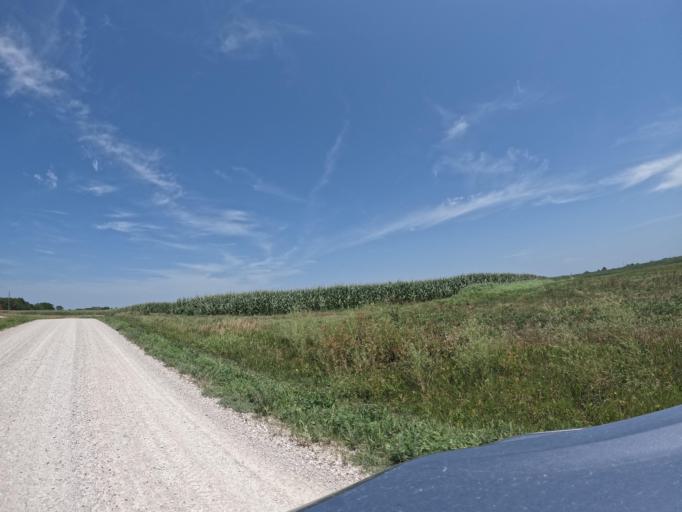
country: US
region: Iowa
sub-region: Henry County
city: Mount Pleasant
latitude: 40.9103
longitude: -91.6549
